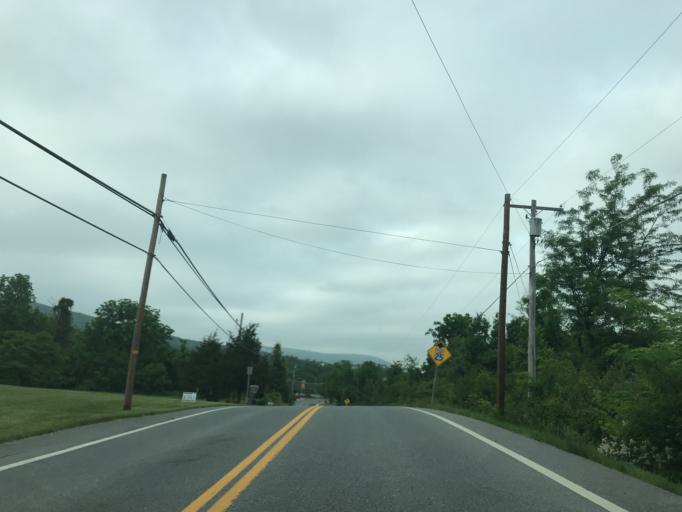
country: US
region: Maryland
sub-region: Frederick County
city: Thurmont
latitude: 39.6107
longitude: -77.4193
